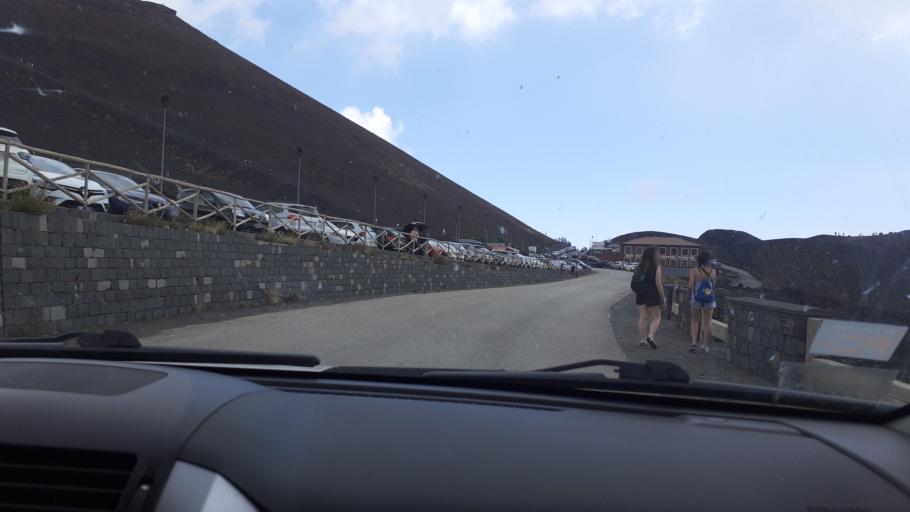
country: IT
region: Sicily
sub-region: Catania
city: Nicolosi
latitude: 37.6990
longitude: 15.0018
